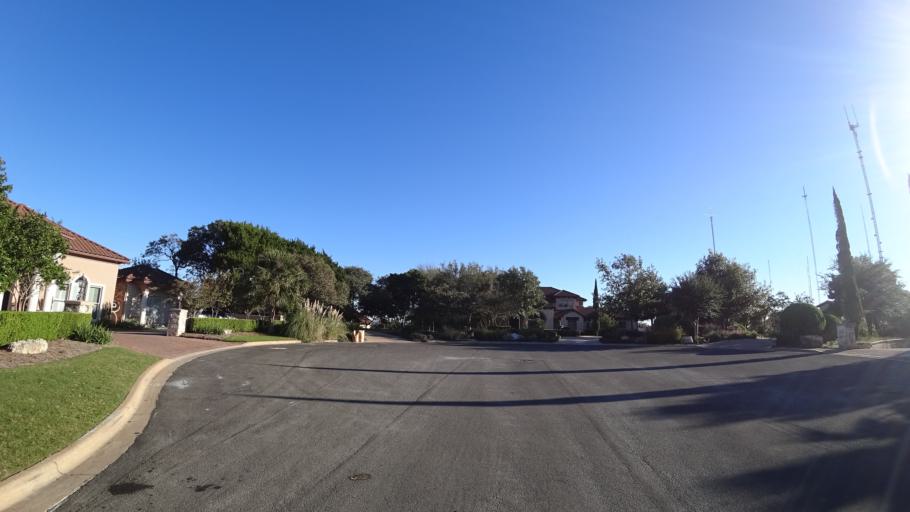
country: US
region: Texas
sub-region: Travis County
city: West Lake Hills
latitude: 30.3219
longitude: -97.8108
